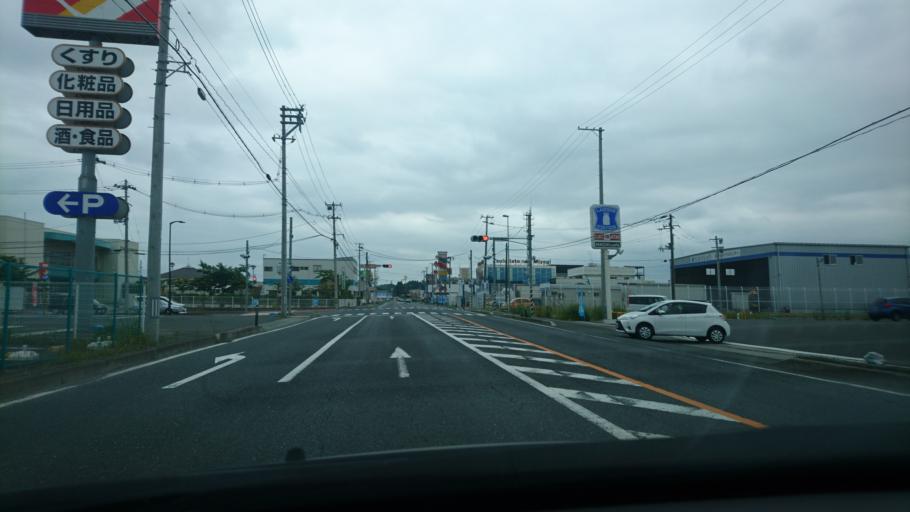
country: JP
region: Miyagi
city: Furukawa
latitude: 38.7469
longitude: 141.0146
